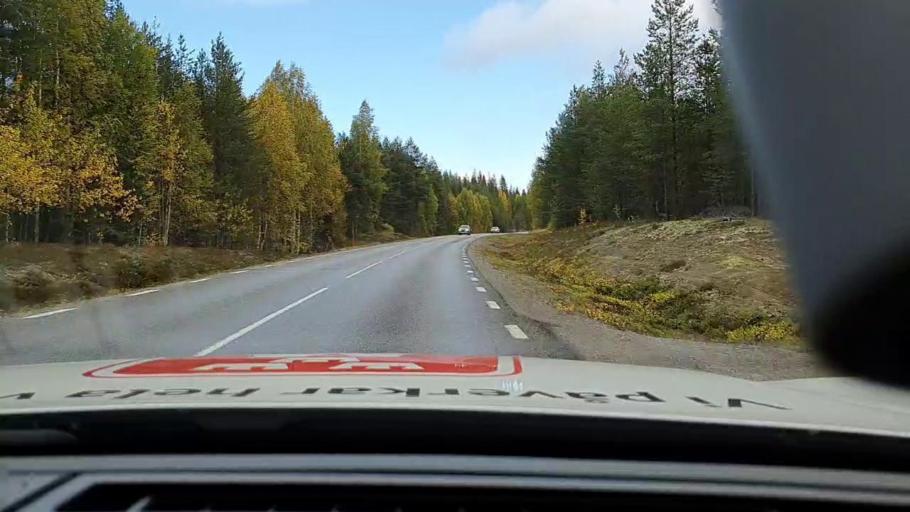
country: SE
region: Vaesterbotten
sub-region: Norsjo Kommun
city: Norsjoe
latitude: 64.9639
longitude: 19.6980
